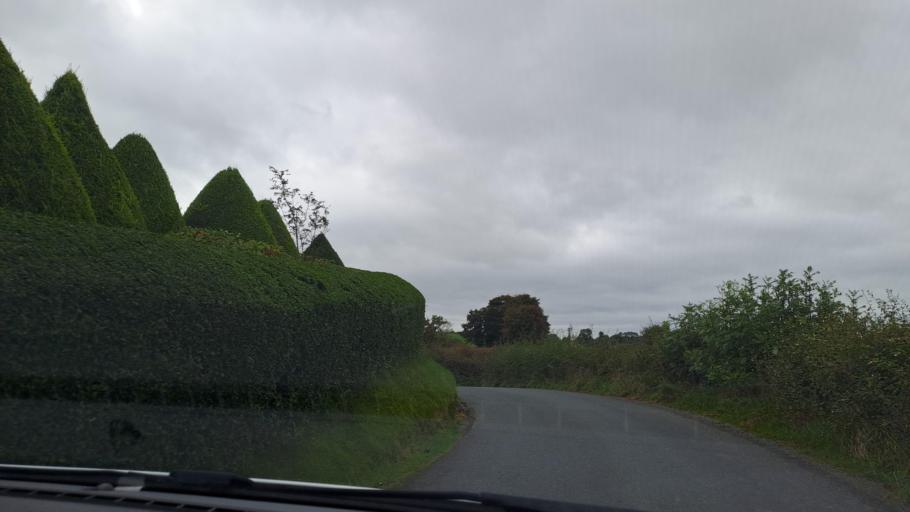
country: IE
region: Ulster
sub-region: An Cabhan
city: Kingscourt
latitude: 54.0164
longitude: -6.8759
